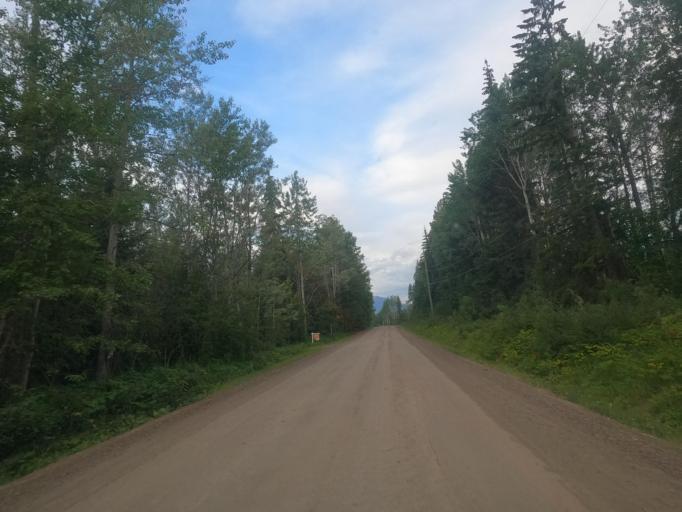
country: CA
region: British Columbia
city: Golden
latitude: 51.4458
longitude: -117.0136
